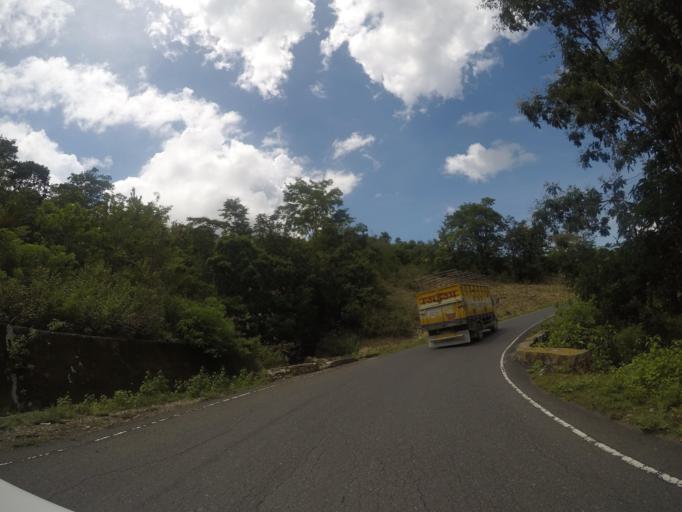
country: TL
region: Bobonaro
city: Maliana
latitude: -8.9525
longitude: 125.1083
